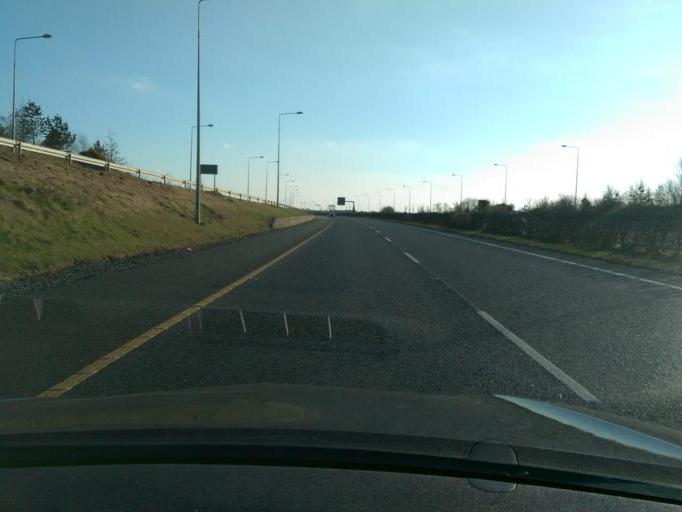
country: IE
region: Leinster
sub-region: Laois
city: Portlaoise
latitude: 53.0486
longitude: -7.2405
